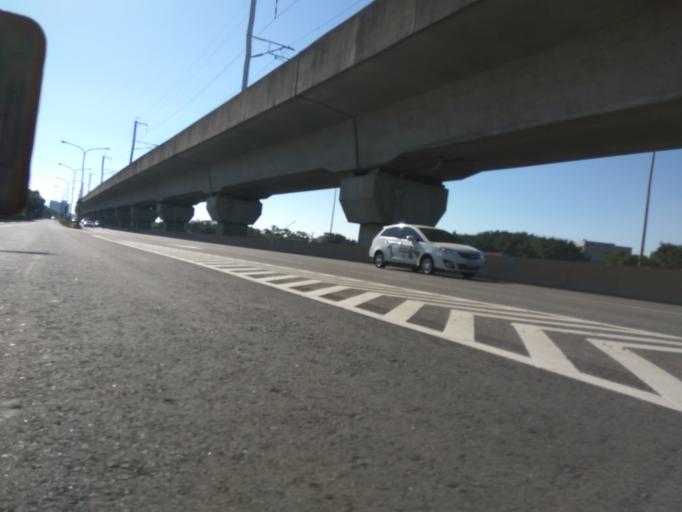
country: TW
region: Taiwan
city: Taoyuan City
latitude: 24.9717
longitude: 121.1742
